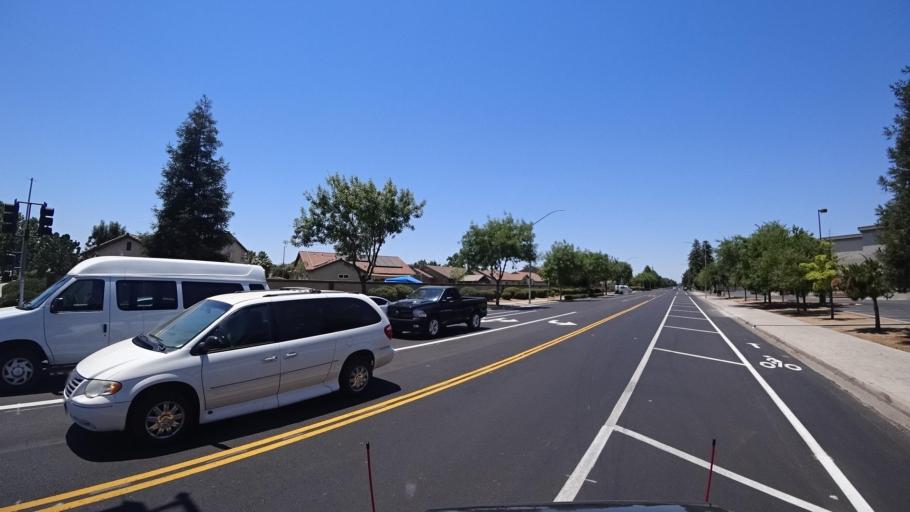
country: US
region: California
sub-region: Fresno County
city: Sunnyside
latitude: 36.7323
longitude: -119.7187
